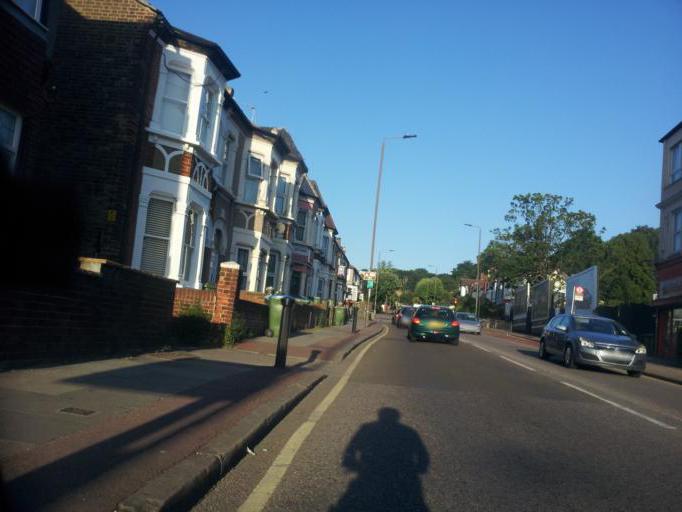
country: GB
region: England
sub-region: Greater London
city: Abbey Wood
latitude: 51.4849
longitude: 0.1055
